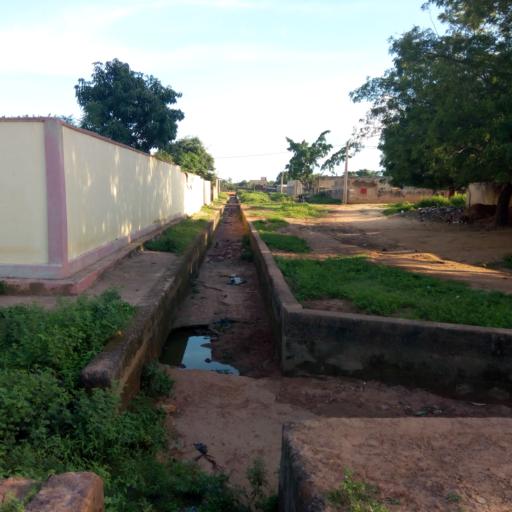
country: ML
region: Sikasso
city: Koutiala
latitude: 12.4093
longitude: -5.4488
